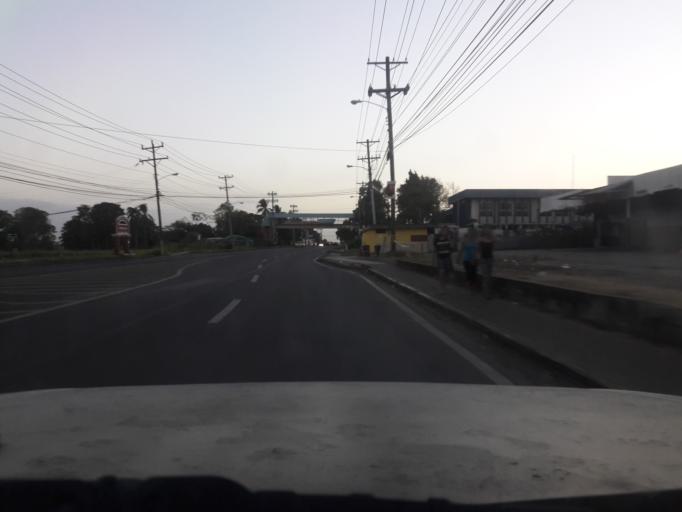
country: PA
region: Panama
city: San Miguelito
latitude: 9.0562
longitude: -79.4339
